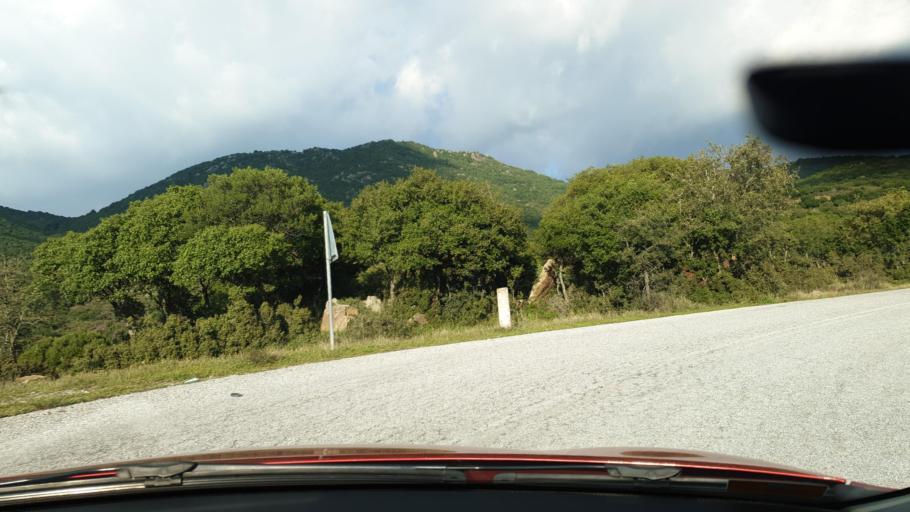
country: GR
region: Central Macedonia
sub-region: Nomos Thessalonikis
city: Peristera
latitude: 40.5254
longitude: 23.1870
